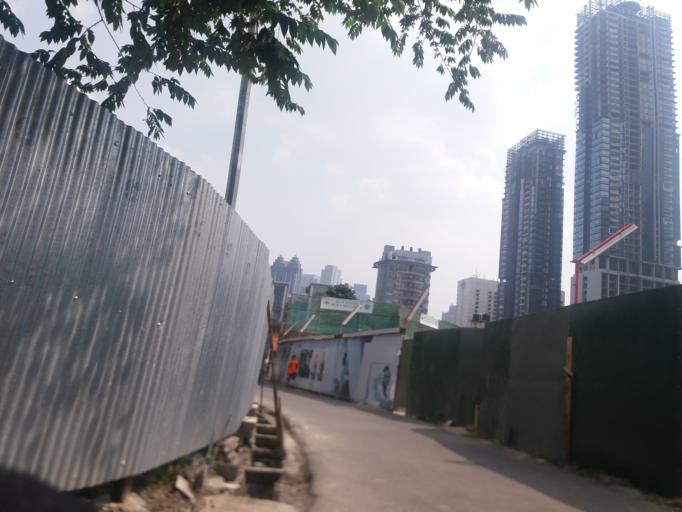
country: ID
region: Jakarta Raya
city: Jakarta
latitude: -6.2213
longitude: 106.8189
